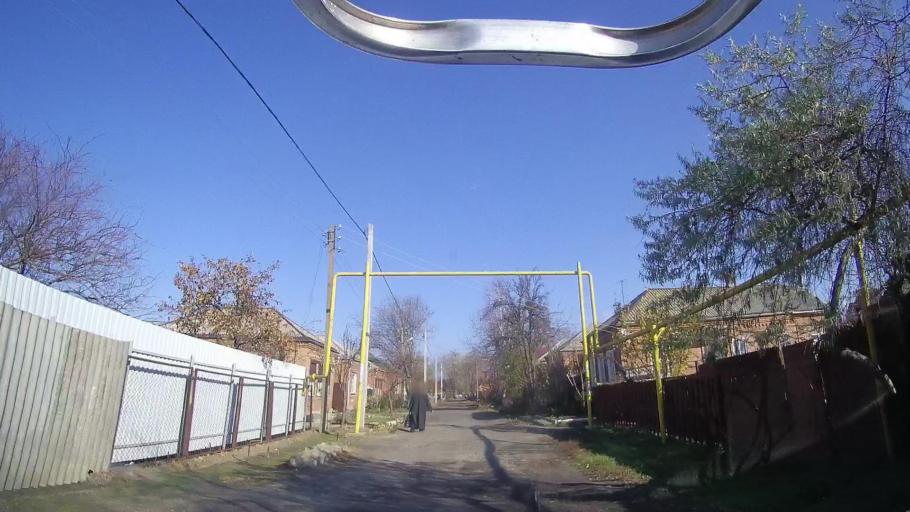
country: RU
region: Rostov
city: Bataysk
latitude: 47.1162
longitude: 39.6852
